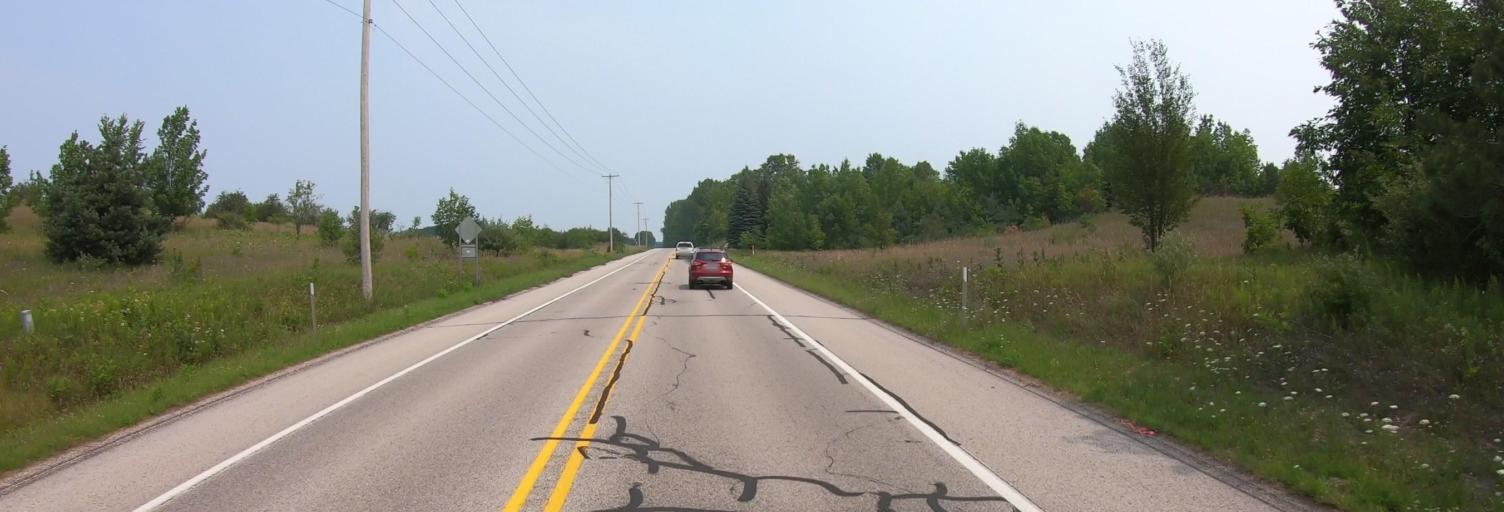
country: US
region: Michigan
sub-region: Leelanau County
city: Leland
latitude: 45.0873
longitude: -85.6691
